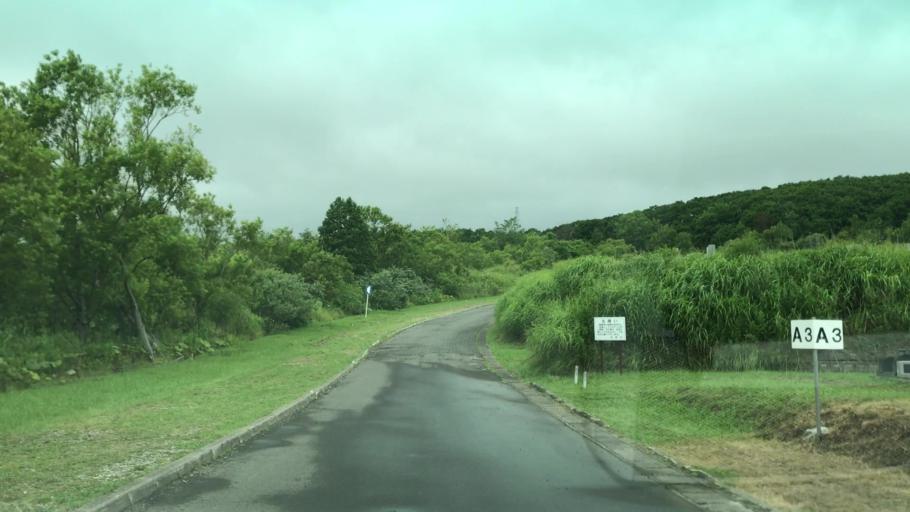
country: JP
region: Hokkaido
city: Muroran
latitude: 42.3940
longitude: 140.9999
